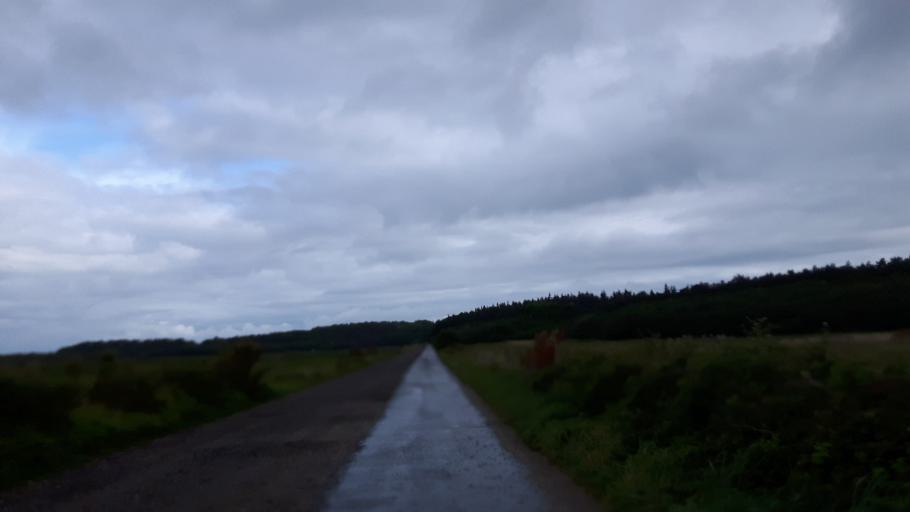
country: NL
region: Friesland
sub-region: Gemeente Ameland
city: Nes
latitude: 53.4472
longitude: 5.7575
